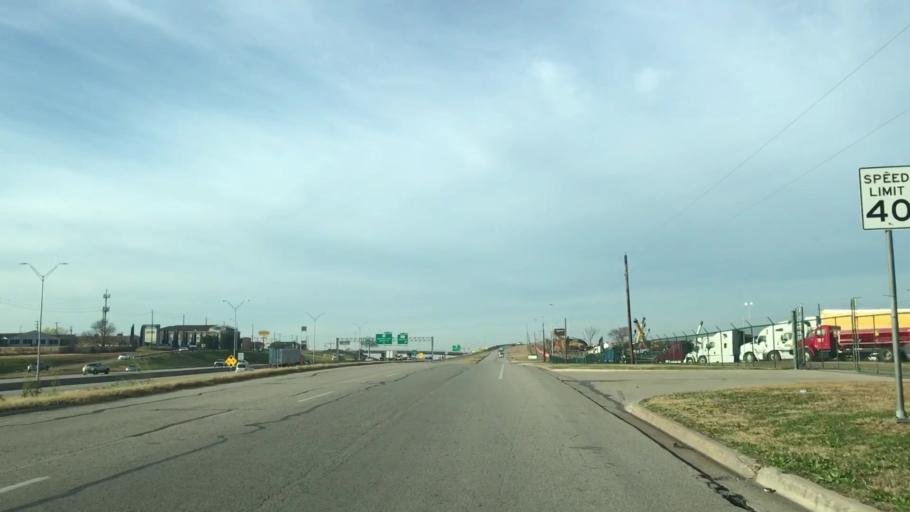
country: US
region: Texas
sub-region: Tarrant County
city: Sansom Park
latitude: 32.8178
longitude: -97.4056
